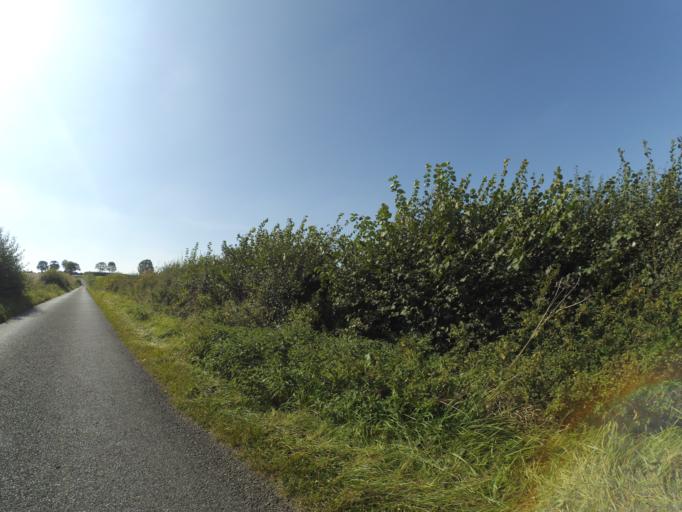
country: GB
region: England
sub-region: Warwickshire
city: Rugby
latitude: 52.4178
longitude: -1.2559
